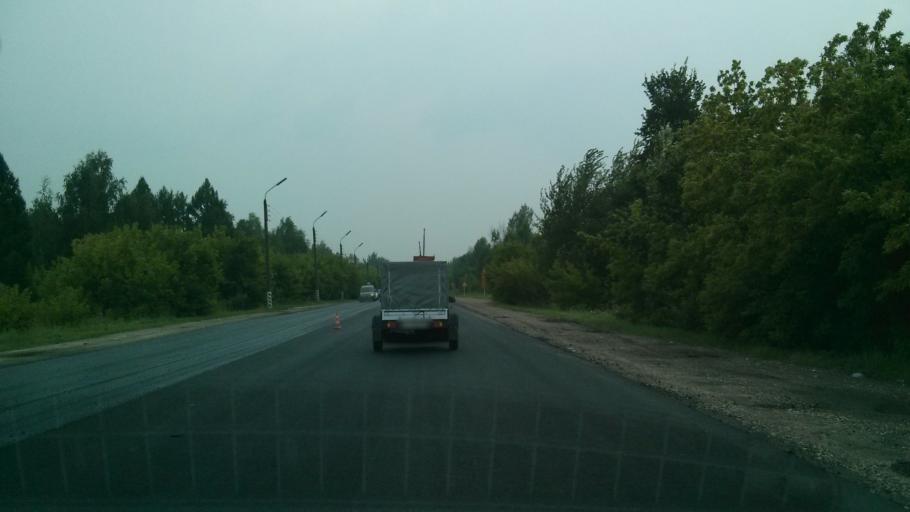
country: RU
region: Nizjnij Novgorod
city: Kstovo
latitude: 56.1133
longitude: 44.1490
